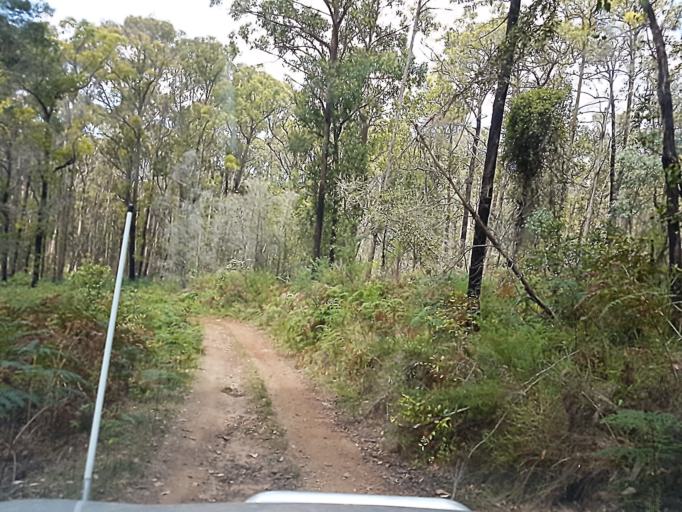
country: AU
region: Victoria
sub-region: East Gippsland
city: Lakes Entrance
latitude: -37.3468
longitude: 148.3570
